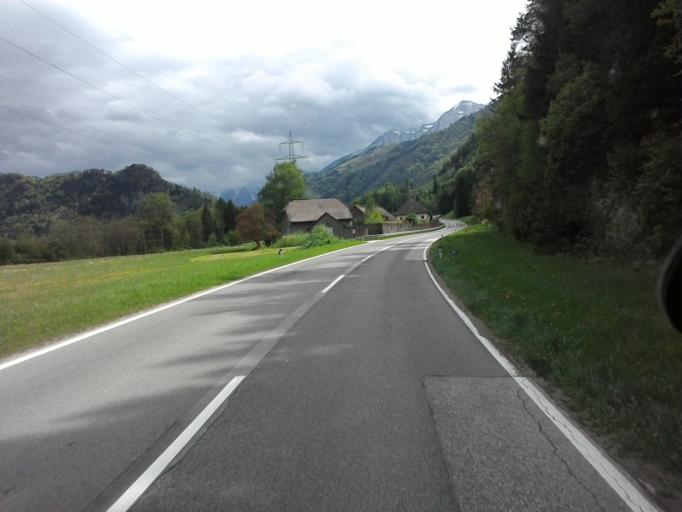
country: AT
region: Upper Austria
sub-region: Politischer Bezirk Kirchdorf an der Krems
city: Micheldorf in Oberoesterreich
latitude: 47.7988
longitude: 14.1626
